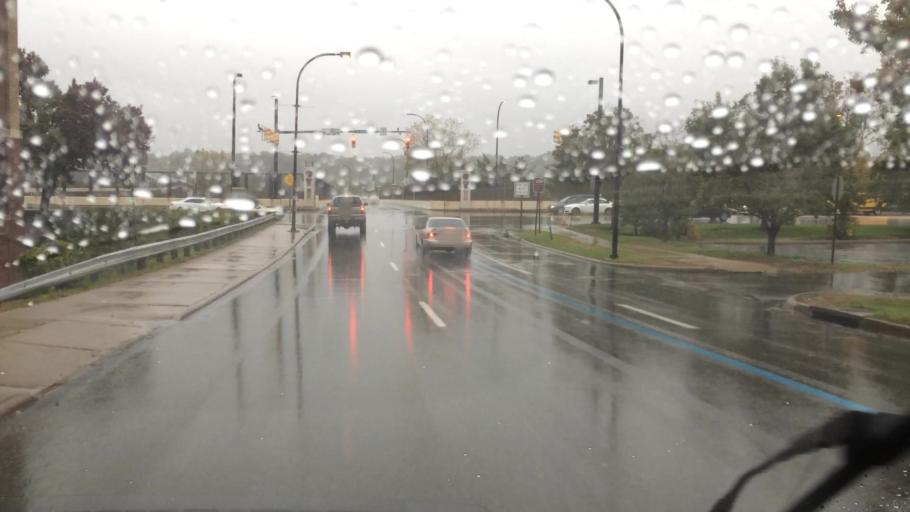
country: US
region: Ohio
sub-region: Summit County
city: Akron
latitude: 41.0860
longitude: -81.5139
